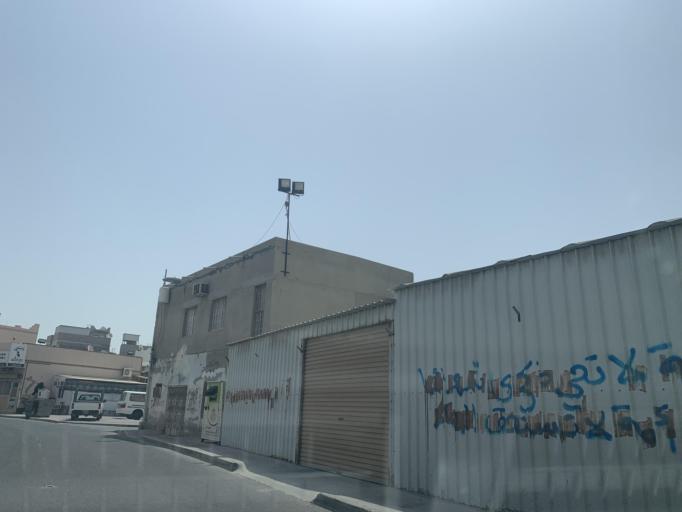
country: BH
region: Northern
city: Madinat `Isa
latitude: 26.1876
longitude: 50.5494
